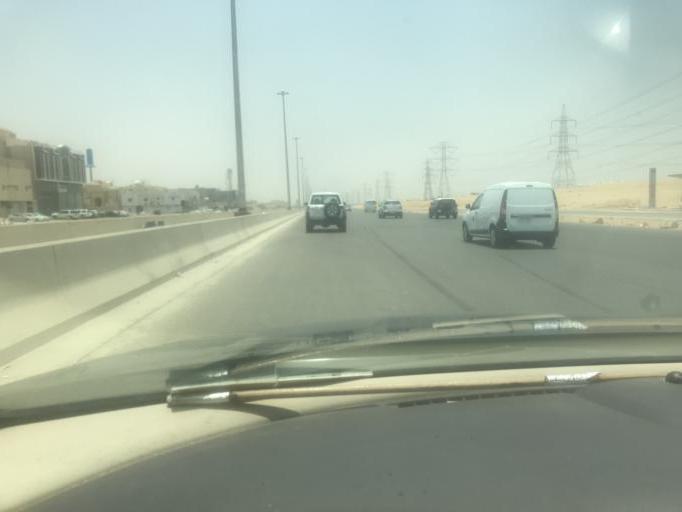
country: SA
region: Ar Riyad
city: Riyadh
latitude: 24.8194
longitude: 46.7388
